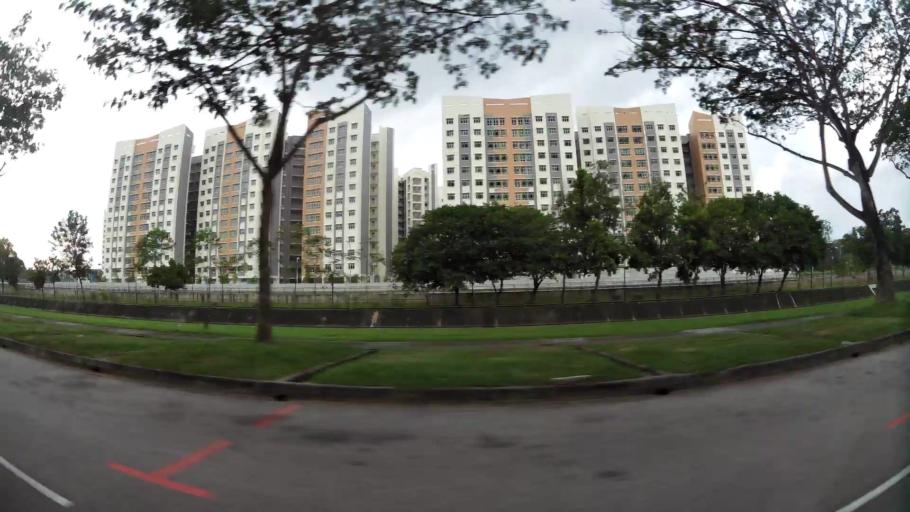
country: MY
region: Johor
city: Kampung Pasir Gudang Baru
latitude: 1.4437
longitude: 103.8342
